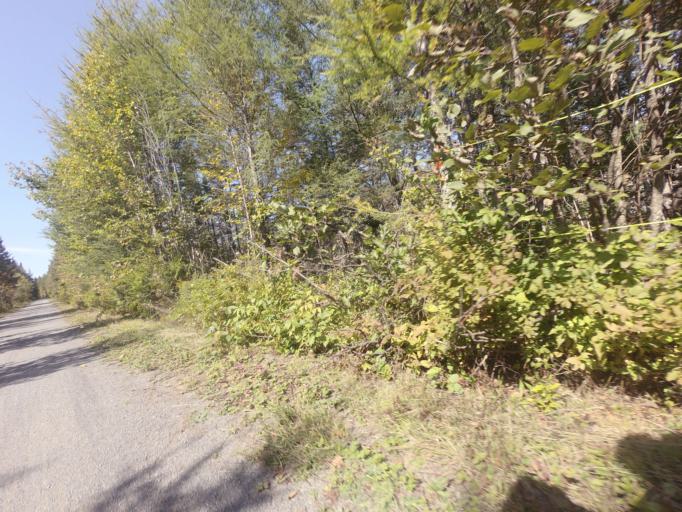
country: CA
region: Quebec
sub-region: Laurentides
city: Sainte-Agathe-des-Monts
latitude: 46.1043
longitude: -74.3842
